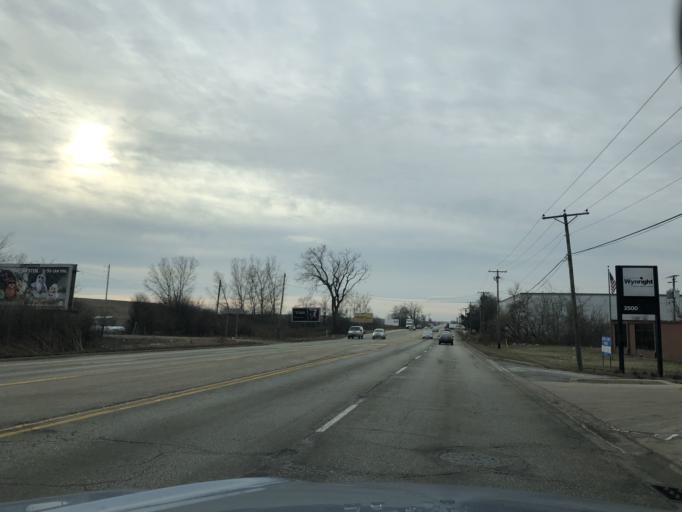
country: US
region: Illinois
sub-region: Cook County
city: Elk Grove Village
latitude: 41.9913
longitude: -87.9400
